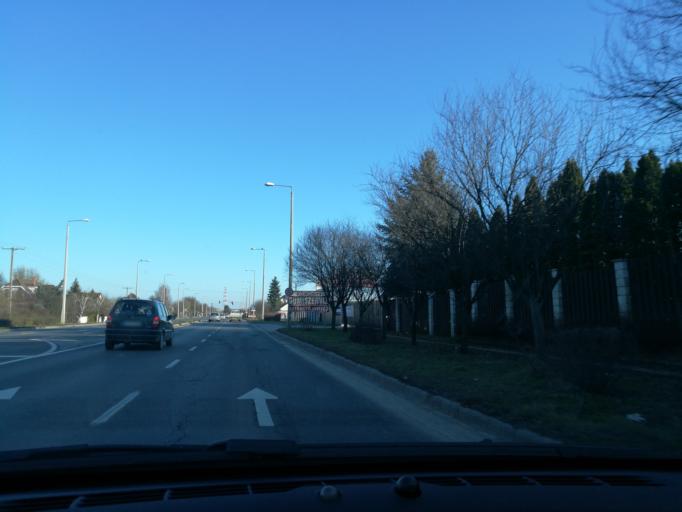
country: HU
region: Szabolcs-Szatmar-Bereg
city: Nyirpazony
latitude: 47.9501
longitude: 21.7768
